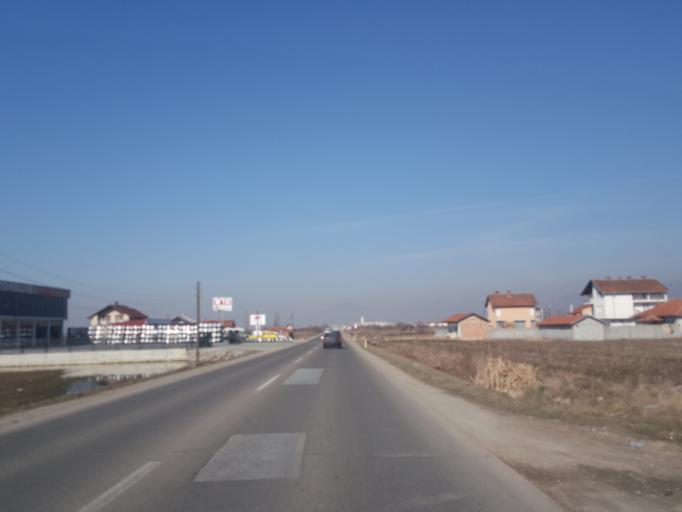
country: XK
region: Mitrovica
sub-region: Vushtrri
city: Vushtrri
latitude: 42.7924
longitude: 21.0028
